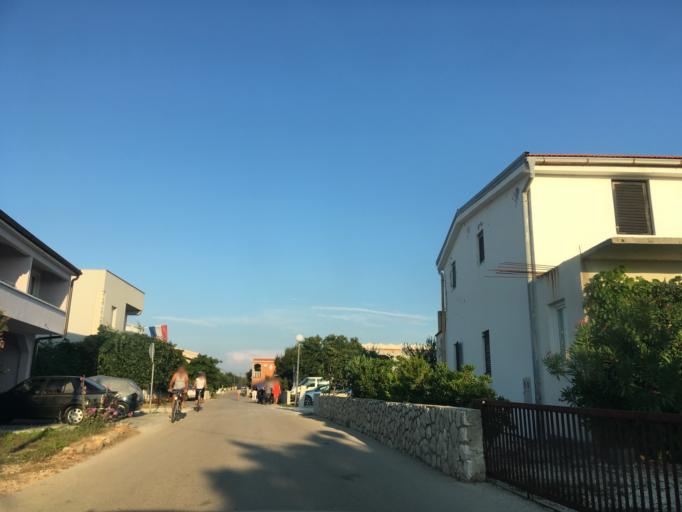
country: HR
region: Zadarska
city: Vir
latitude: 44.3052
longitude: 15.0939
